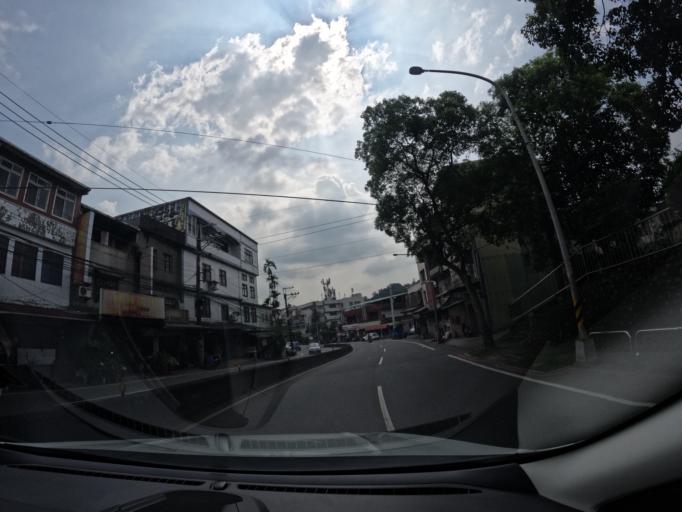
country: TW
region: Taiwan
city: Daxi
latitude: 24.9065
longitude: 121.3613
